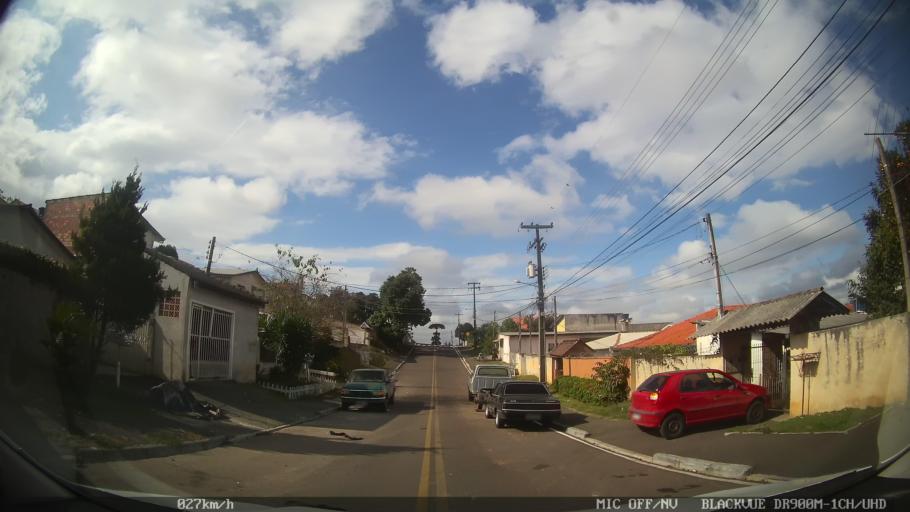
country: BR
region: Parana
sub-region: Colombo
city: Colombo
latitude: -25.3572
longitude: -49.1877
